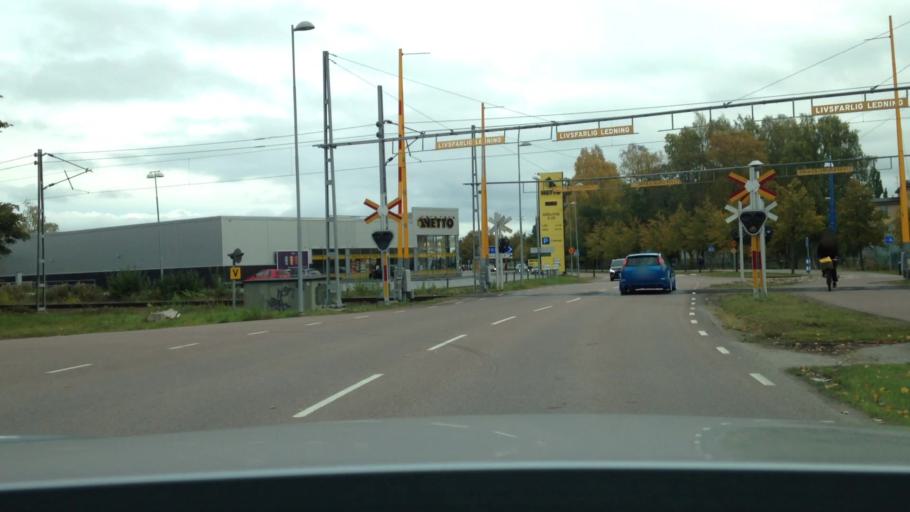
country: SE
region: Vaermland
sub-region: Karlstads Kommun
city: Karlstad
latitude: 59.3810
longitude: 13.4690
